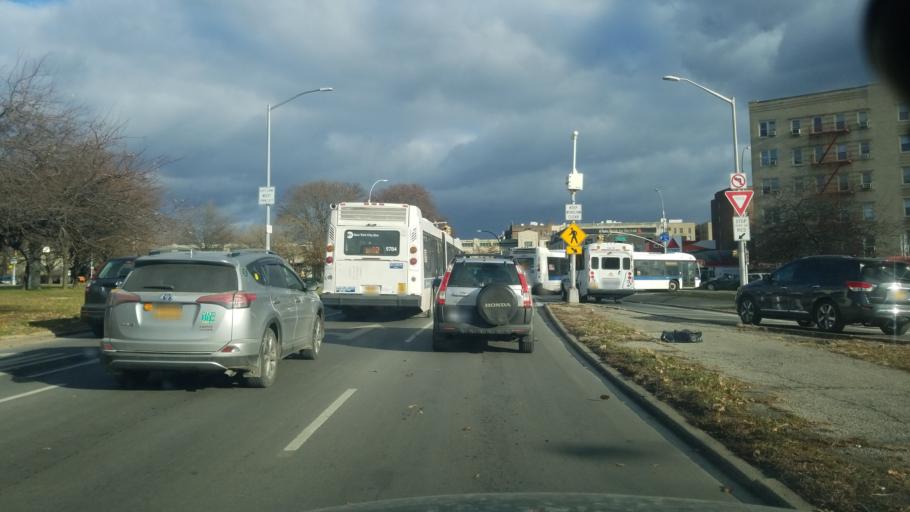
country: US
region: New York
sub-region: Bronx
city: The Bronx
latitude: 40.8567
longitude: -73.8703
